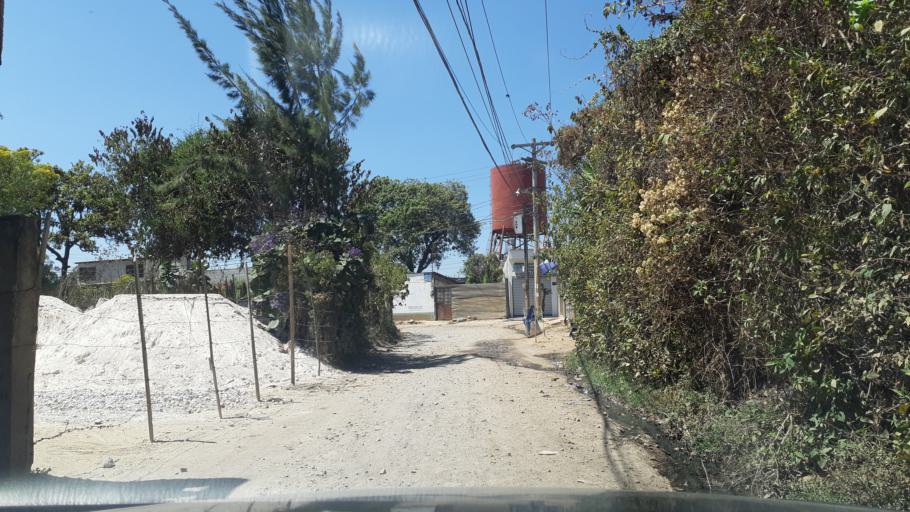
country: GT
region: Chimaltenango
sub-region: Municipio de Chimaltenango
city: Chimaltenango
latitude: 14.6534
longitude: -90.8103
